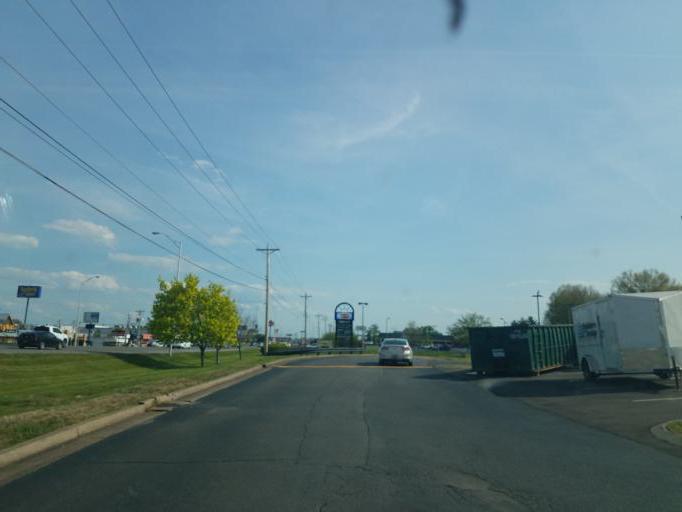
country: US
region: Kentucky
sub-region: Warren County
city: Bowling Green
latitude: 36.9534
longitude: -86.4267
